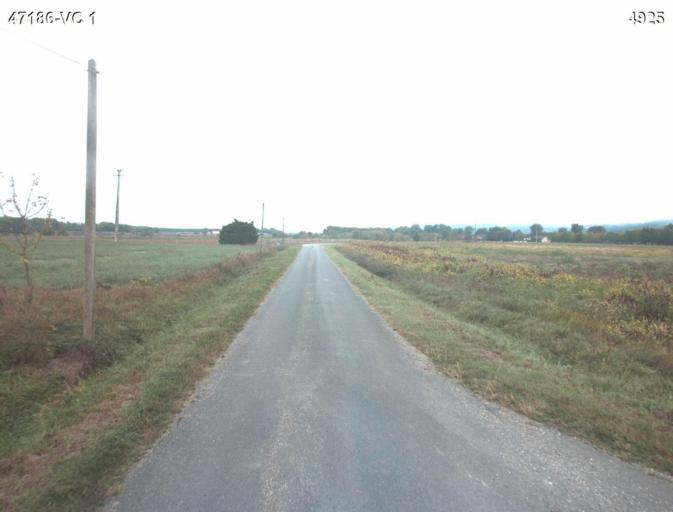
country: FR
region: Aquitaine
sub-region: Departement du Lot-et-Garonne
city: Port-Sainte-Marie
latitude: 44.2280
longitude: 0.4368
